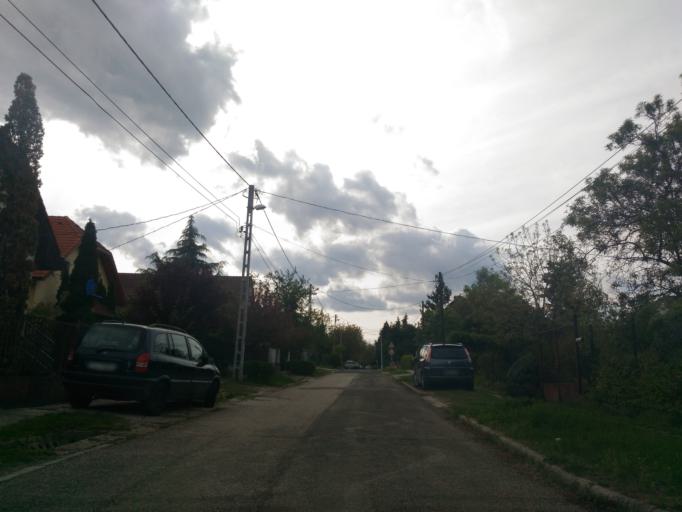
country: HU
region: Budapest
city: Budapest XXII. keruelet
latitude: 47.4289
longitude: 19.0160
